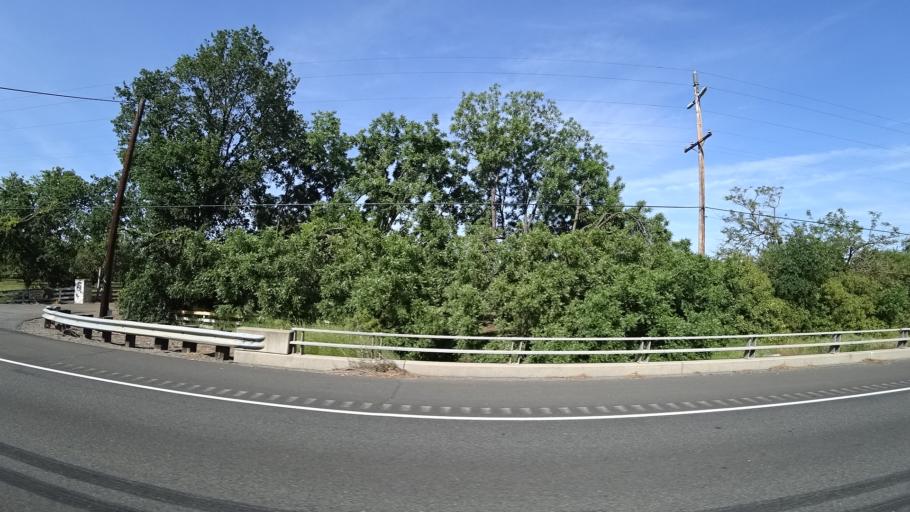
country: US
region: California
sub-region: Glenn County
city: Hamilton City
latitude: 39.8808
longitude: -121.9731
